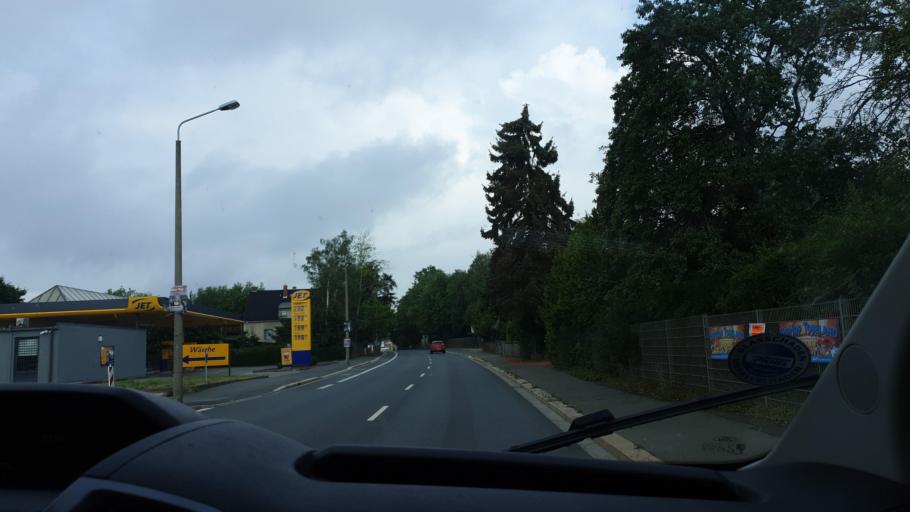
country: DE
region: Saxony
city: Reichenbach/Vogtland
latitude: 50.6286
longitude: 12.3004
